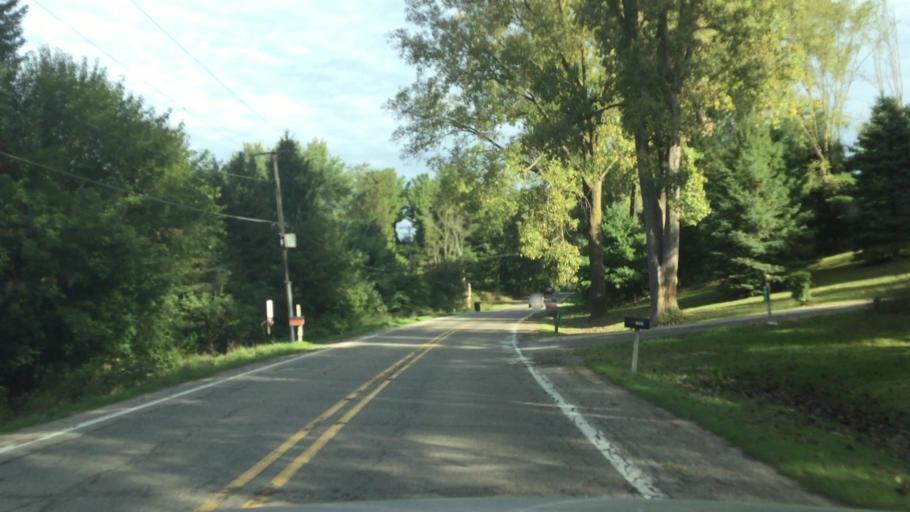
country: US
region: Michigan
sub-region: Livingston County
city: Brighton
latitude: 42.4854
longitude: -83.8516
